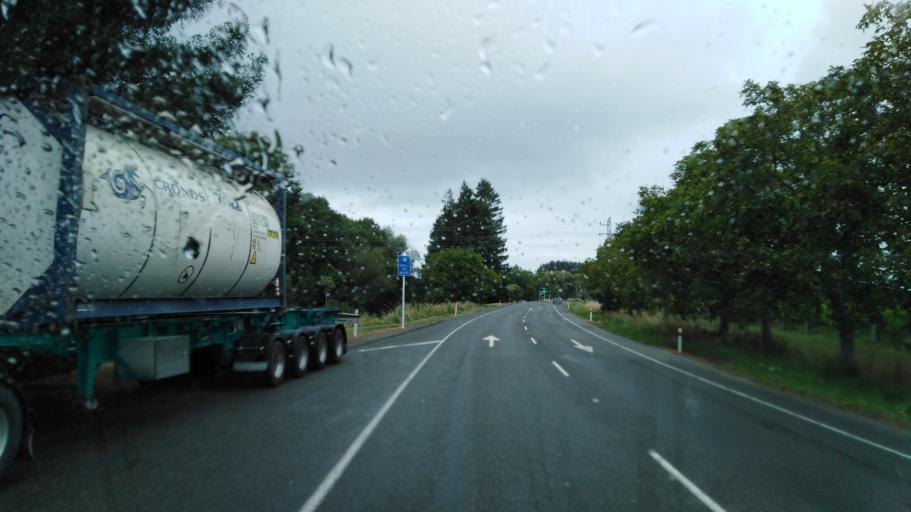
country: NZ
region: Marlborough
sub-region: Marlborough District
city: Blenheim
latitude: -41.4585
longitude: 173.9570
